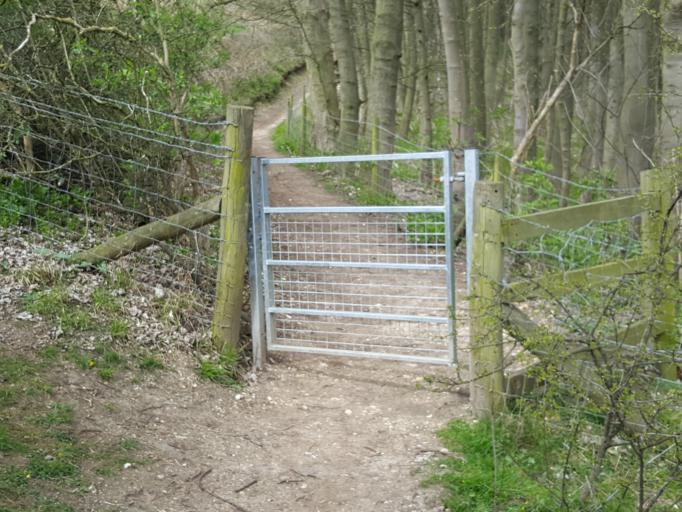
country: GB
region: England
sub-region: East Riding of Yorkshire
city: Brantingham
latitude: 53.7655
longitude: -0.5806
